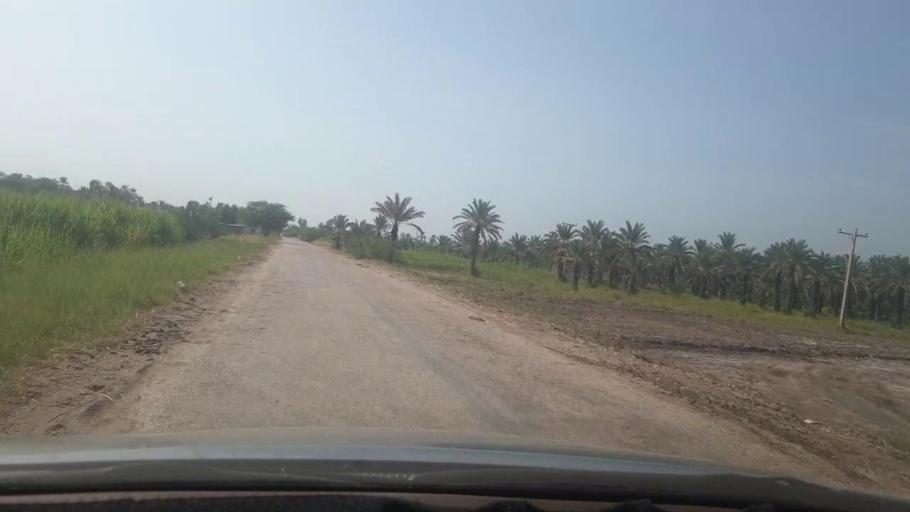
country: PK
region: Sindh
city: Gambat
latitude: 27.3217
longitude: 68.5551
